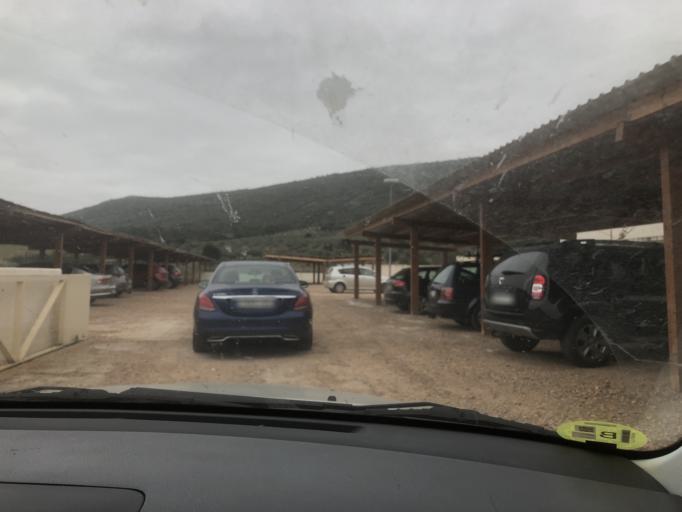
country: ES
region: Castille-La Mancha
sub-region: Provincia de Ciudad Real
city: Navalpino
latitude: 39.3245
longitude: -4.6253
